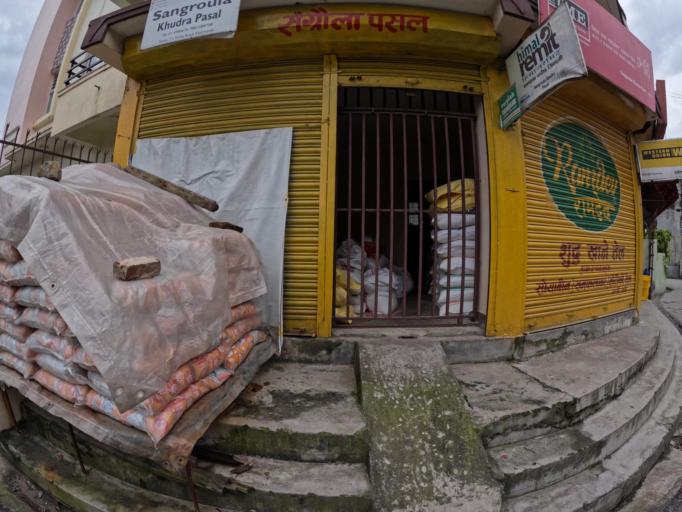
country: NP
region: Central Region
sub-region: Bagmati Zone
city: Kathmandu
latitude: 27.7438
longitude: 85.3211
